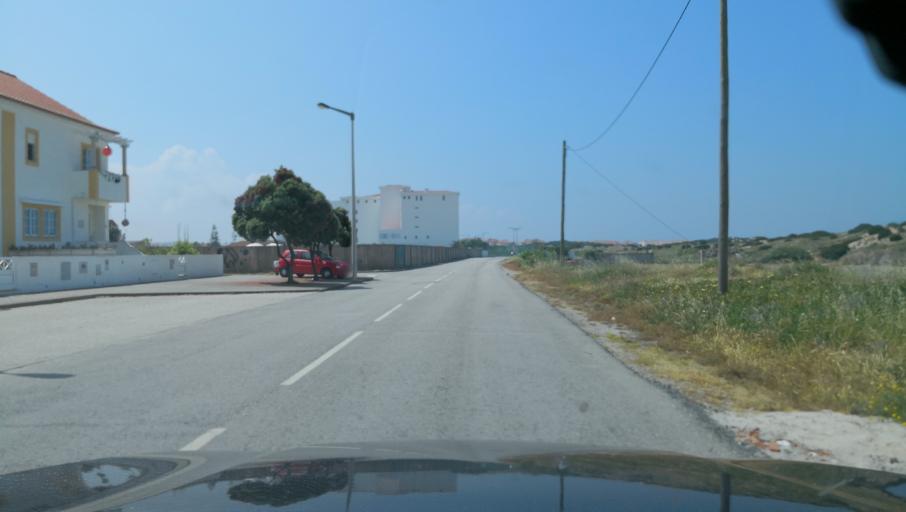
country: PT
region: Leiria
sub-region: Peniche
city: Atouguia da Baleia
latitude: 39.3375
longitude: -9.3542
